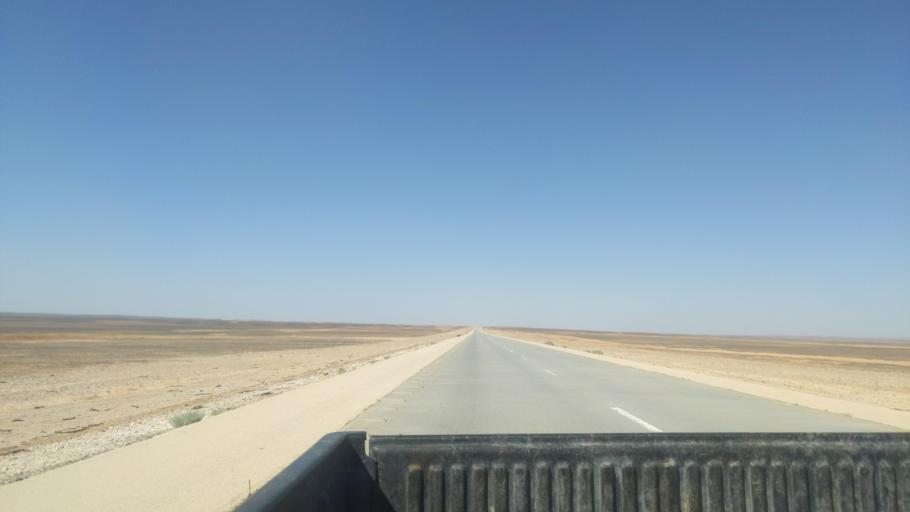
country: JO
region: Amman
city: Al Azraq ash Shamali
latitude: 31.4472
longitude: 36.7643
